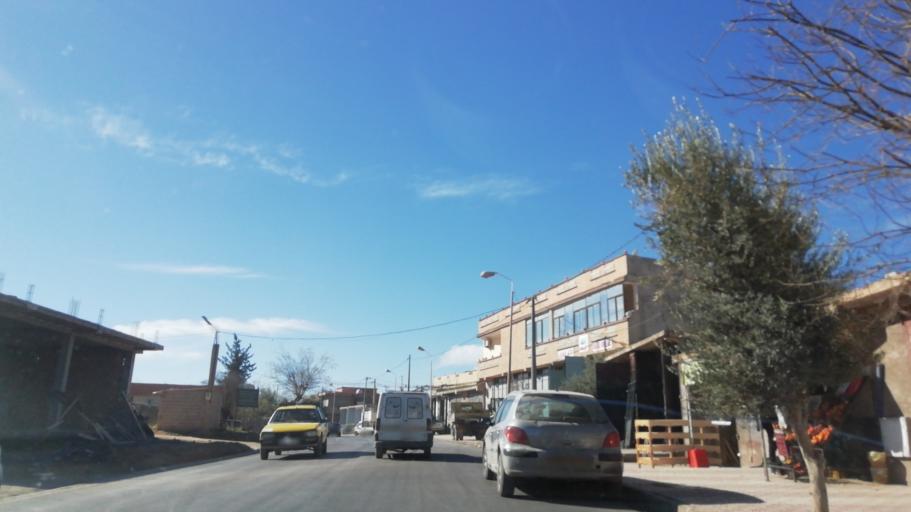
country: DZ
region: Tlemcen
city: Sebdou
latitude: 34.6529
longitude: -1.3174
